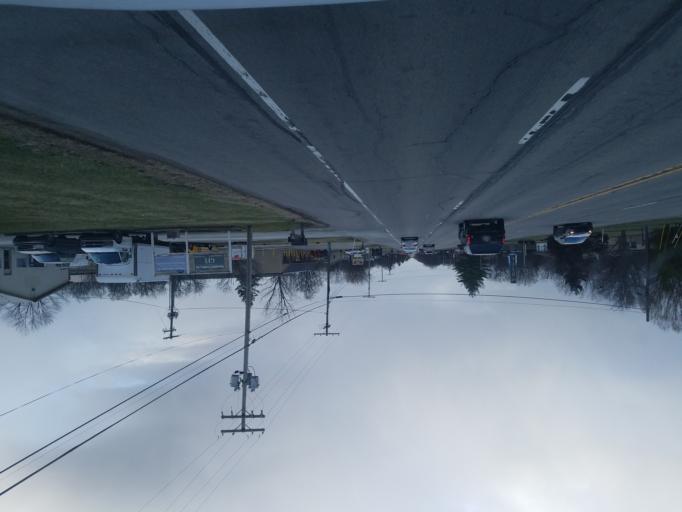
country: US
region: Indiana
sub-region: Hancock County
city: New Palestine
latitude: 39.7806
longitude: -85.8704
